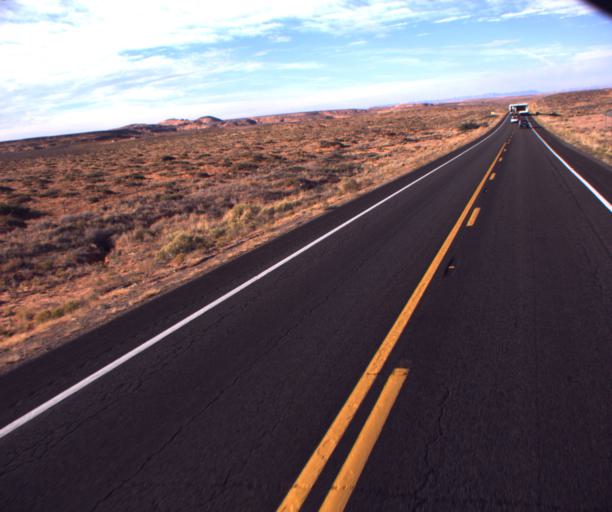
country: US
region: Arizona
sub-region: Apache County
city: Many Farms
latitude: 36.9336
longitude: -109.5659
